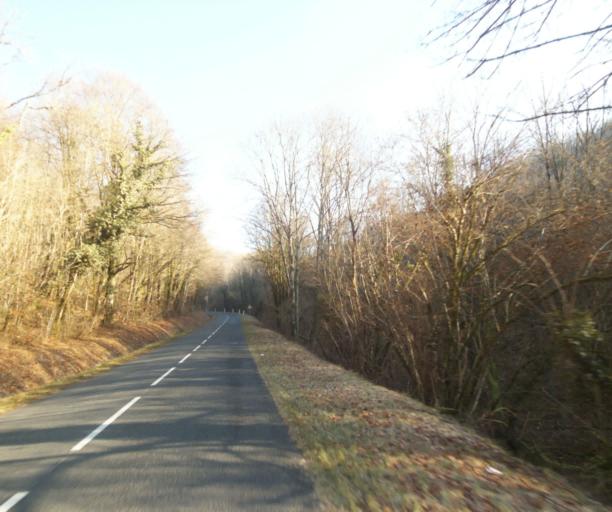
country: FR
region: Champagne-Ardenne
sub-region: Departement de la Haute-Marne
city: Chevillon
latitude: 48.5288
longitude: 5.1772
